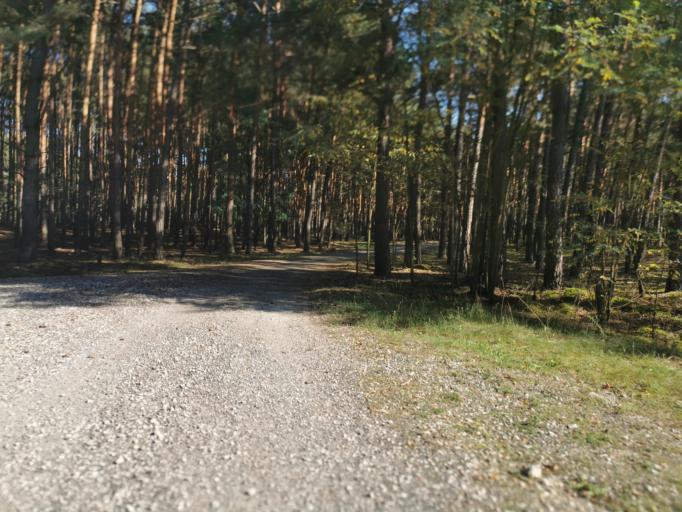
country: SK
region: Trnavsky
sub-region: Okres Senica
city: Senica
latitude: 48.6427
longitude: 17.2435
